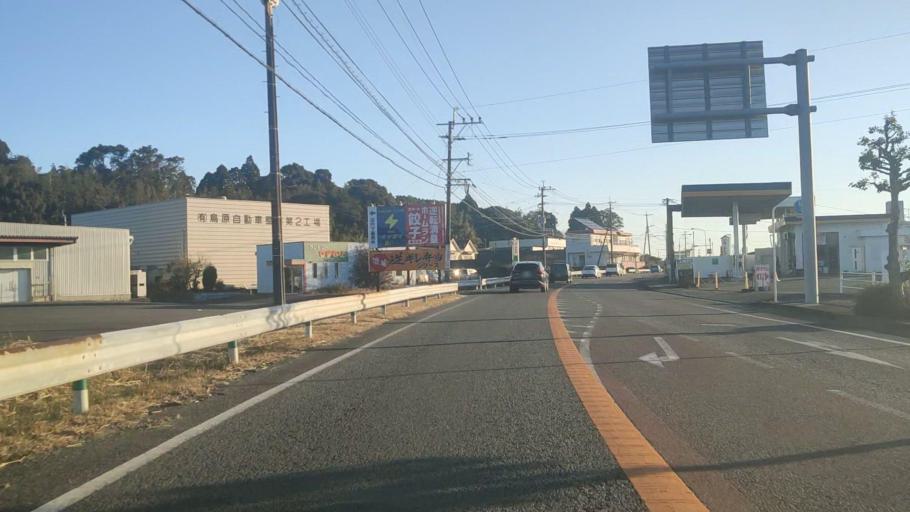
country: JP
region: Miyazaki
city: Takanabe
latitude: 32.0748
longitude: 131.4963
